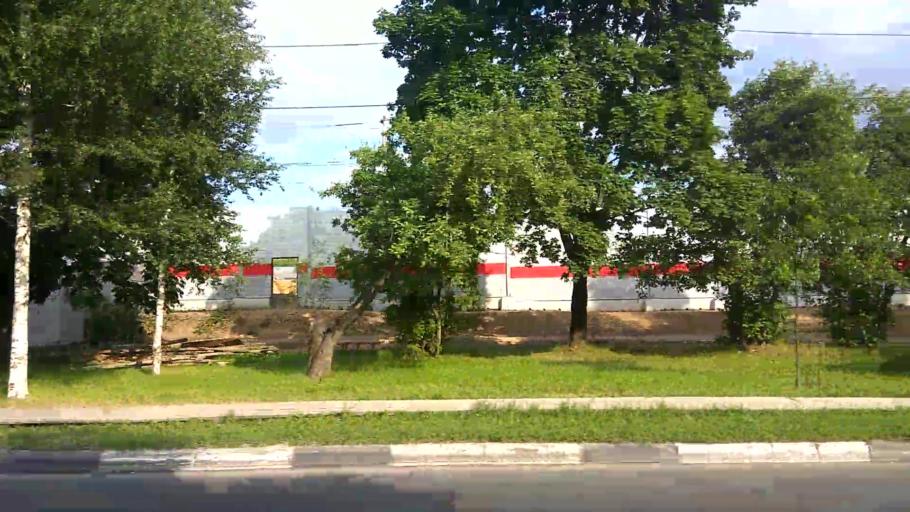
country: RU
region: Moskovskaya
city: Mytishchi
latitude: 55.9222
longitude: 37.7693
